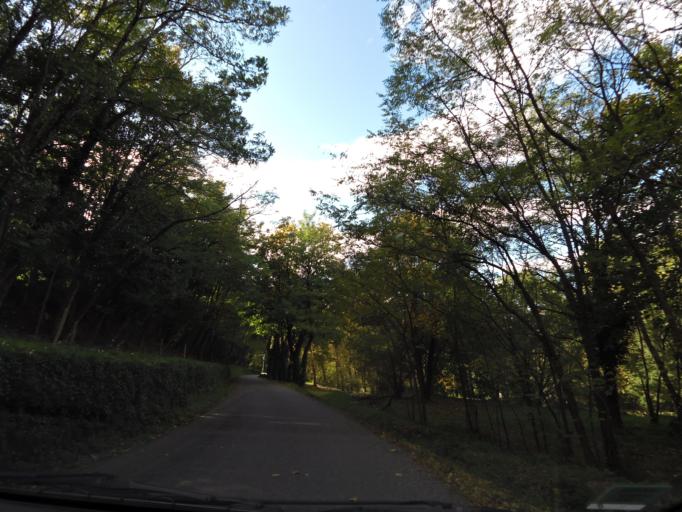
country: FR
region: Languedoc-Roussillon
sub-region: Departement du Gard
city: Lasalle
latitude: 44.0361
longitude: 3.8643
